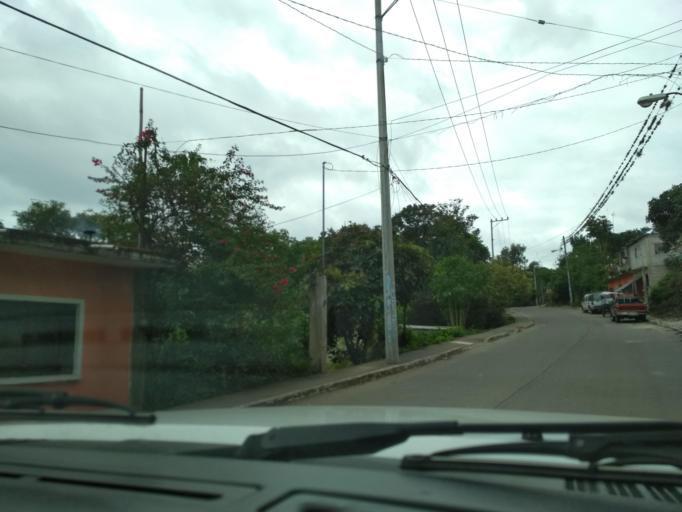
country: MX
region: Veracruz
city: El Castillo
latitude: 19.5768
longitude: -96.8652
